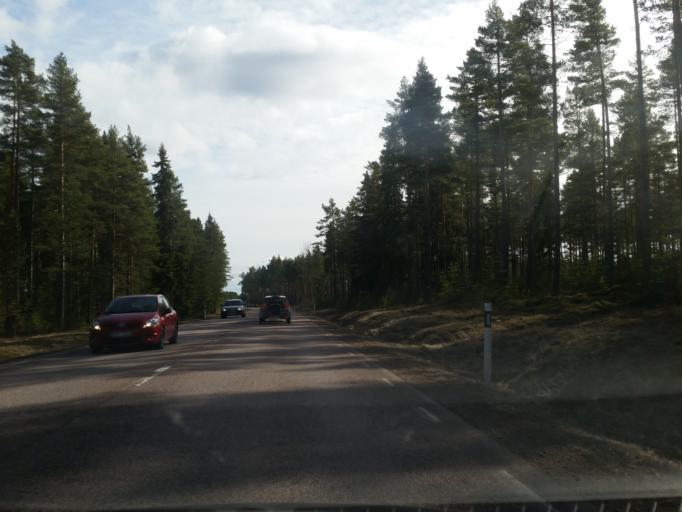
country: SE
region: Dalarna
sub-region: Mora Kommun
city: Mora
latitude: 60.9835
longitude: 14.6878
